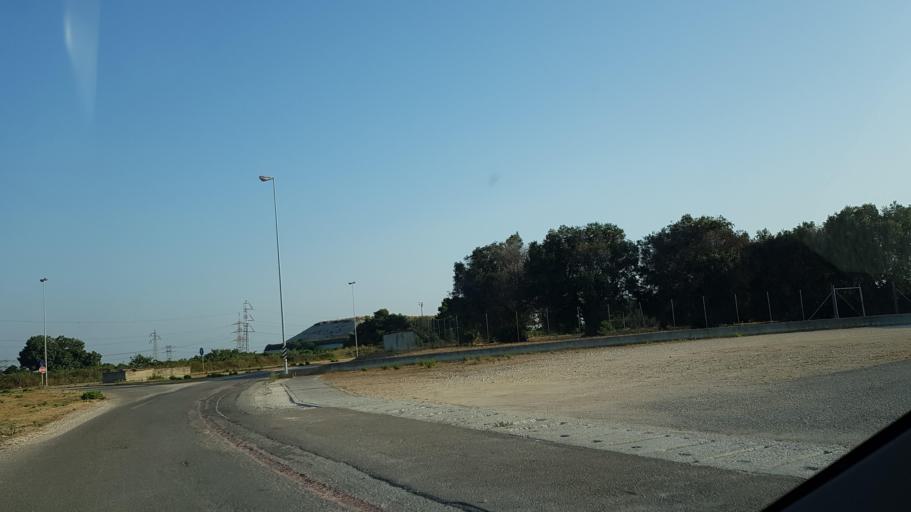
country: IT
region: Apulia
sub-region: Provincia di Brindisi
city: La Rosa
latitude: 40.6235
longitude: 17.9786
